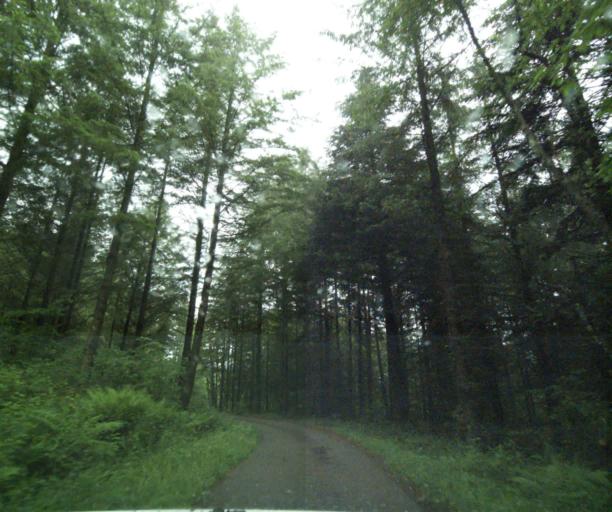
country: FR
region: Bourgogne
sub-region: Departement de Saone-et-Loire
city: Charolles
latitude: 46.3759
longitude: 4.3615
